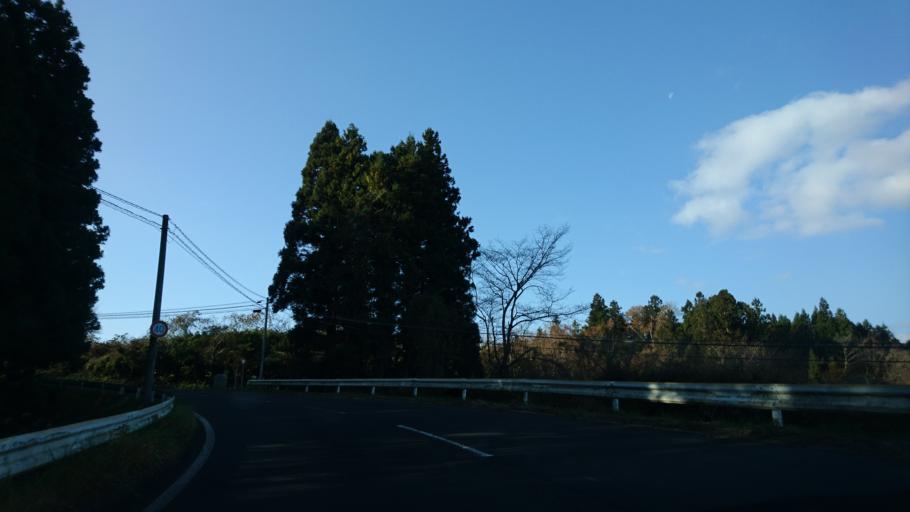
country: JP
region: Iwate
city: Ichinoseki
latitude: 38.8902
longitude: 141.2846
